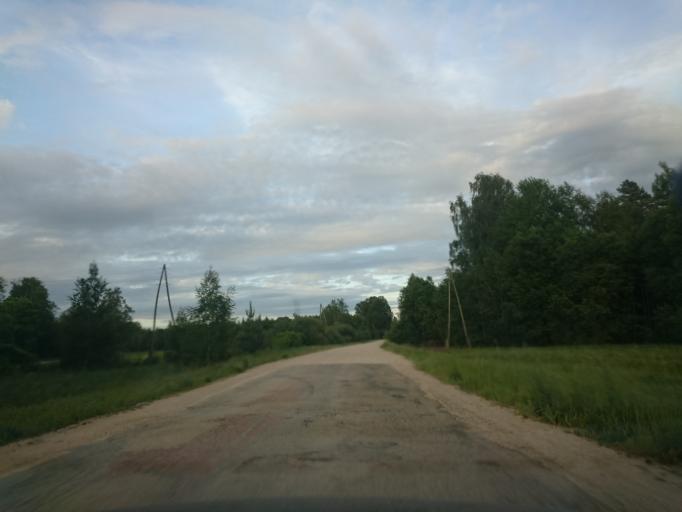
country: LV
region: Ropazu
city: Ropazi
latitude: 56.9579
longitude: 24.7077
